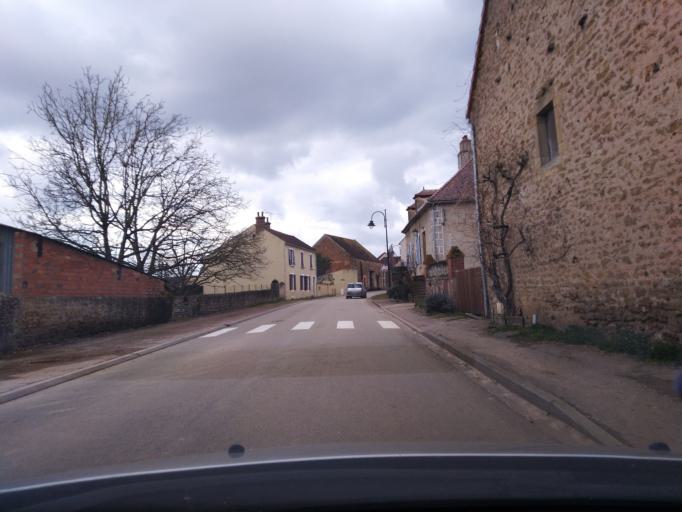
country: FR
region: Bourgogne
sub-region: Departement de l'Yonne
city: Avallon
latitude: 47.5143
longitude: 3.9416
